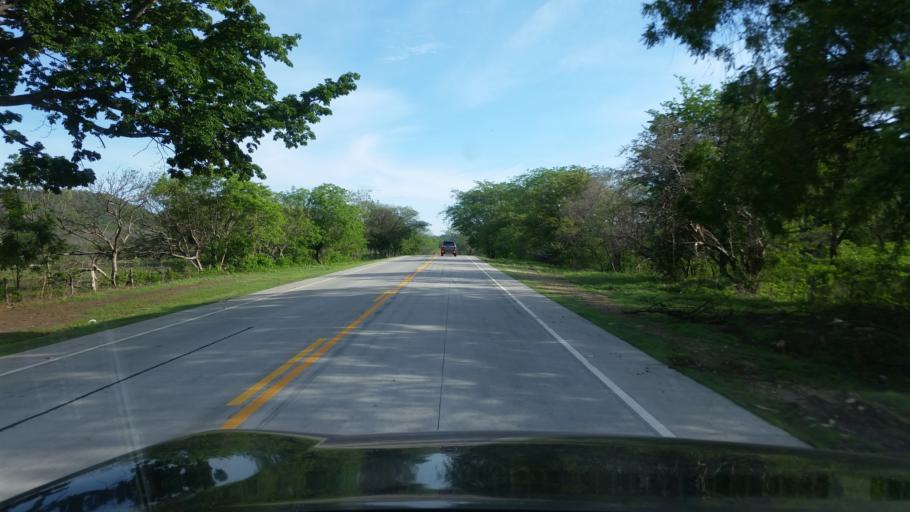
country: NI
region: Leon
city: Nagarote
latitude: 12.1424
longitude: -86.6502
